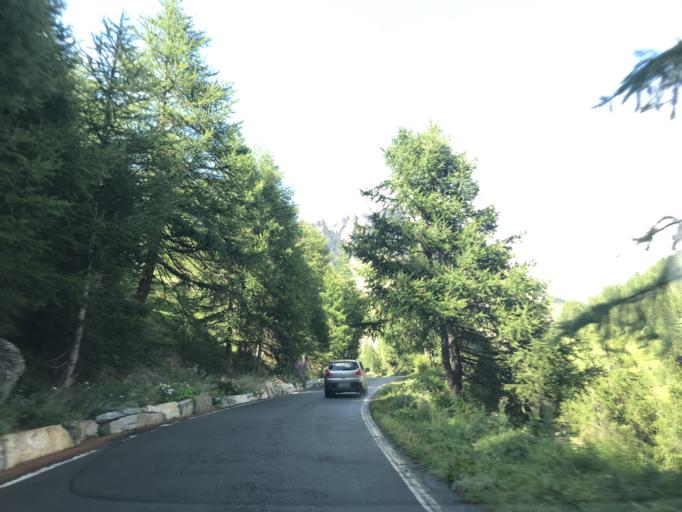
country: IT
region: Piedmont
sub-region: Provincia di Cuneo
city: Pontechianale
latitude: 44.6554
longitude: 6.9892
